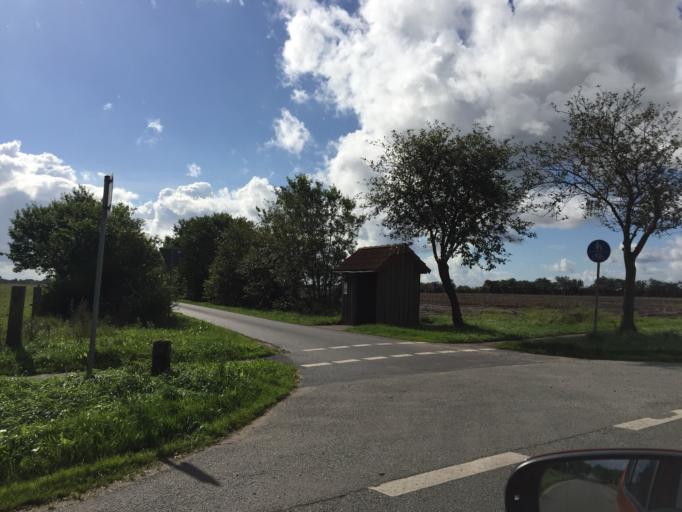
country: DE
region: Schleswig-Holstein
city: Bramstedtlund
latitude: 54.8378
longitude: 9.0582
